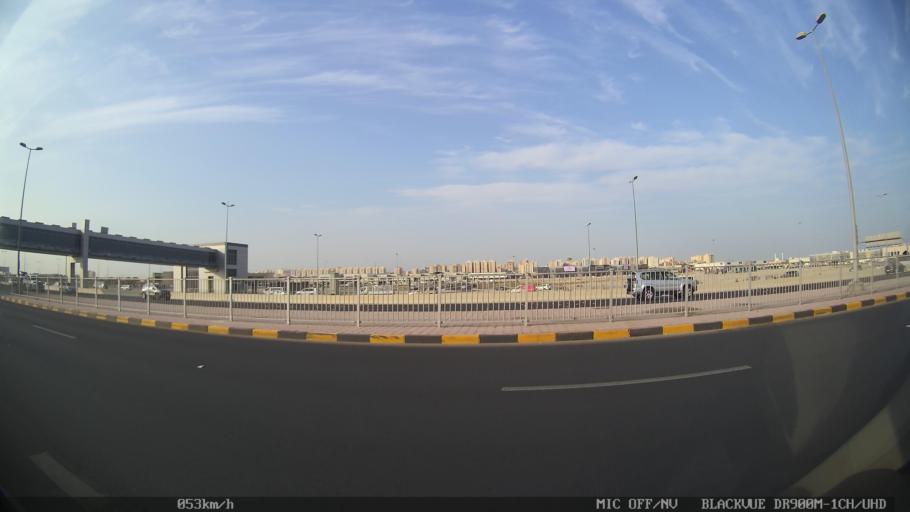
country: KW
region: Al Farwaniyah
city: Janub as Surrah
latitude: 29.2571
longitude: 47.9642
